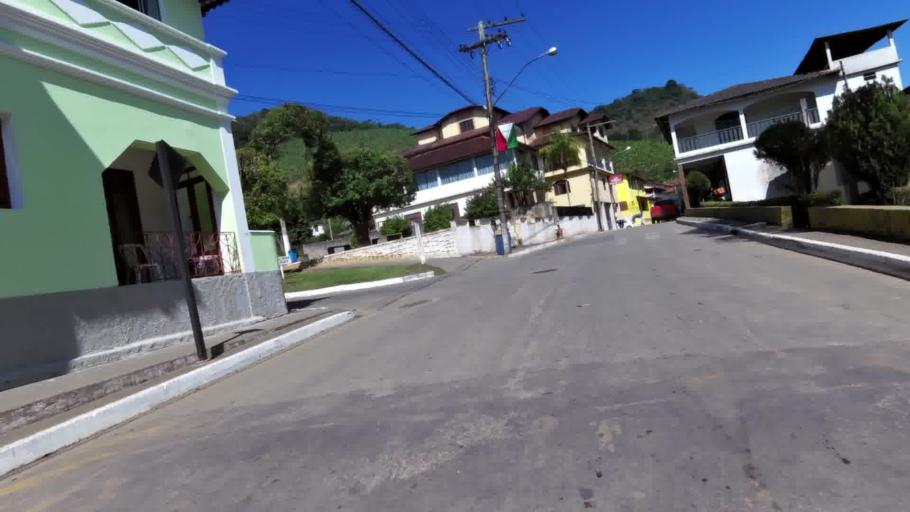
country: BR
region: Espirito Santo
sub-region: Marechal Floriano
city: Marechal Floriano
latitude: -20.4934
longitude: -40.7716
